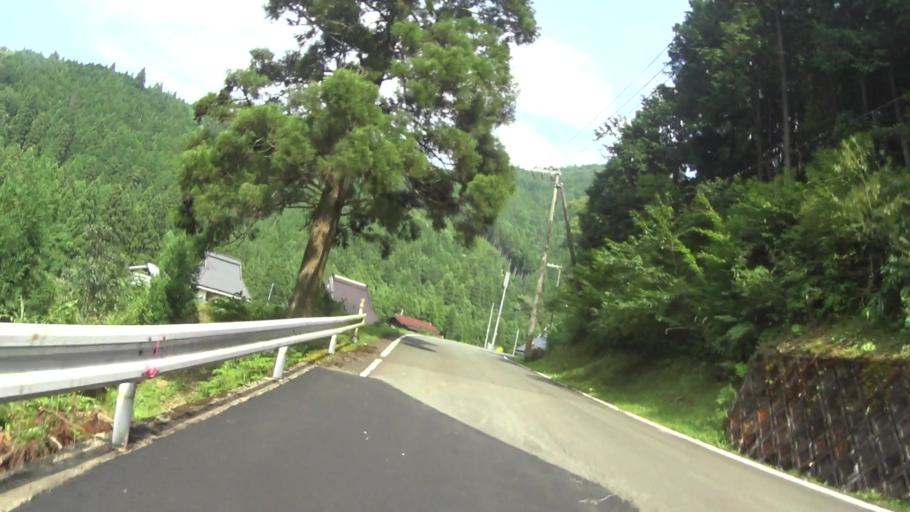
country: JP
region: Fukui
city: Obama
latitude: 35.3086
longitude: 135.6423
